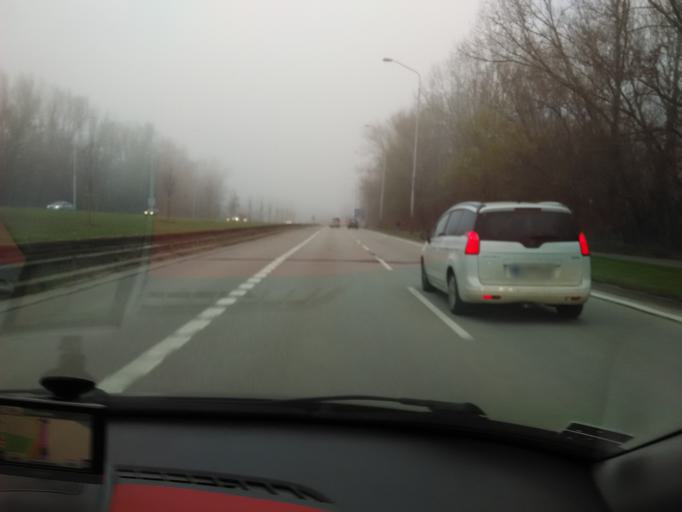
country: SK
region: Bratislavsky
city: Bratislava
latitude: 48.1138
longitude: 17.1307
